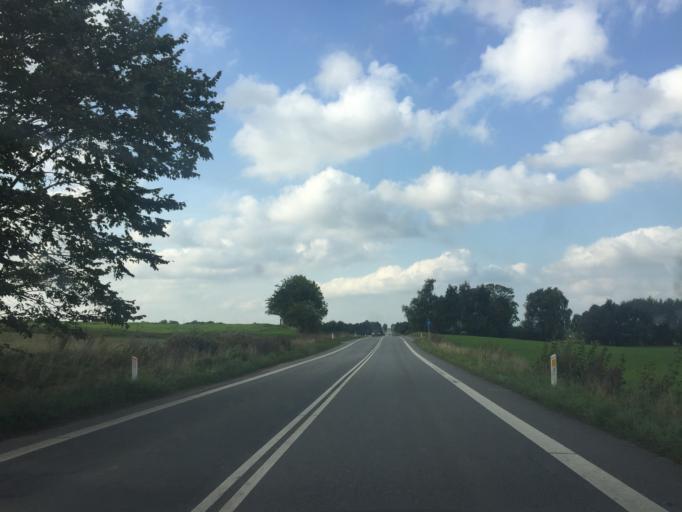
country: DK
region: Zealand
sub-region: Holbaek Kommune
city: Tollose
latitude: 55.6370
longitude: 11.7881
